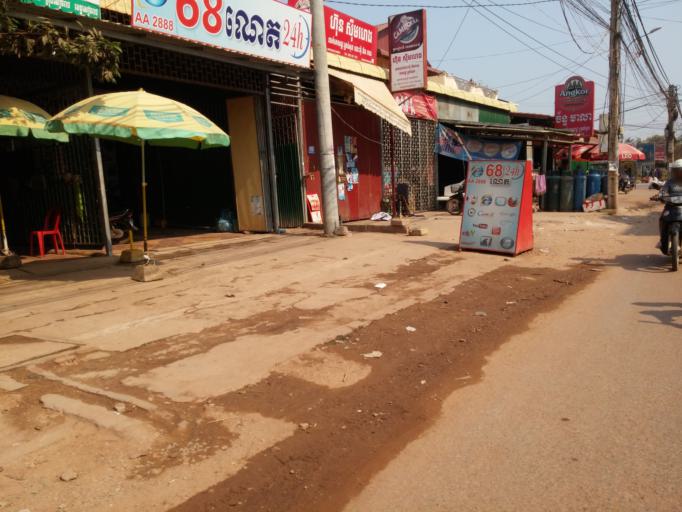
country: KH
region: Siem Reap
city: Siem Reap
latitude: 13.3812
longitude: 103.8519
